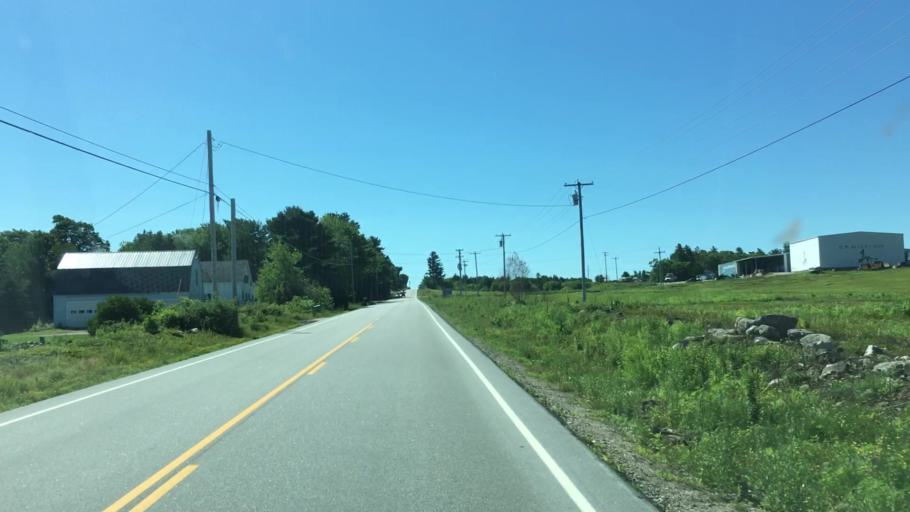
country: US
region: Maine
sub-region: Hancock County
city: Orland
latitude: 44.5516
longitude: -68.6927
